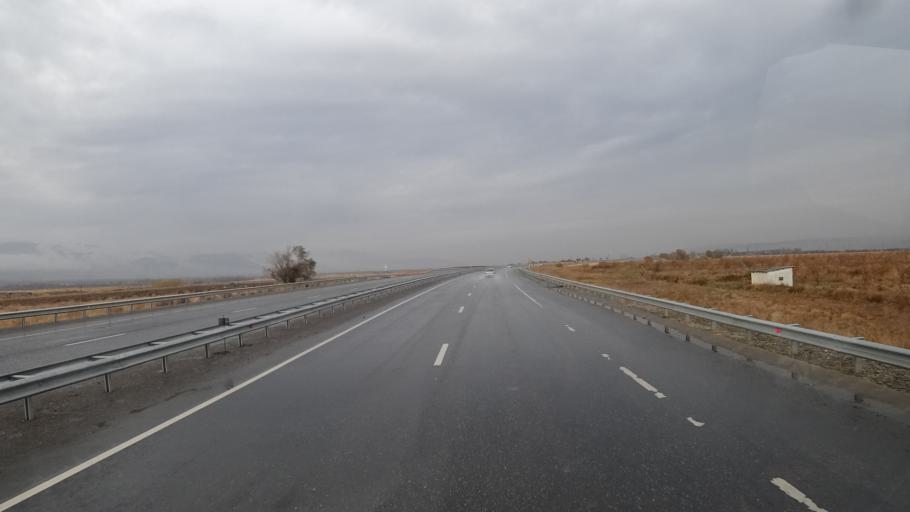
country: KZ
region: Ongtustik Qazaqstan
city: Turar Ryskulov
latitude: 42.5151
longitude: 70.3359
